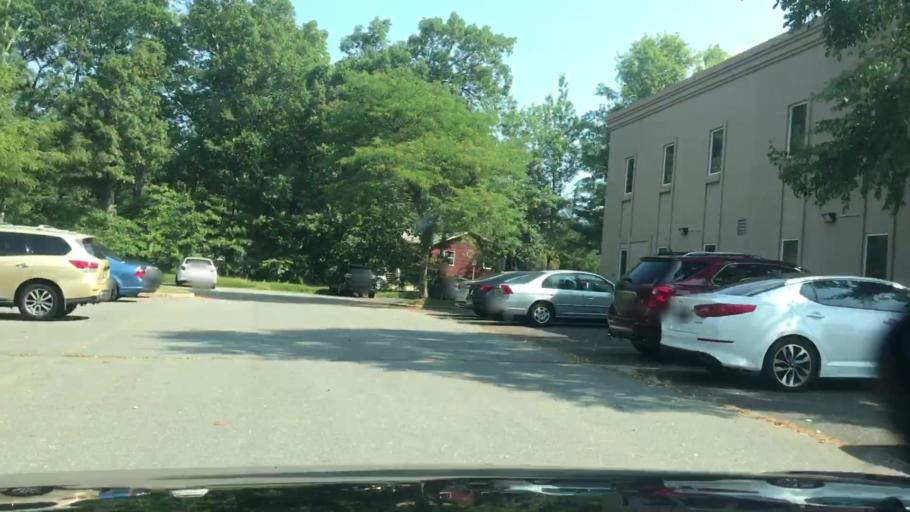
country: US
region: New Jersey
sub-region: Ocean County
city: Toms River
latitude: 39.9881
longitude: -74.1797
